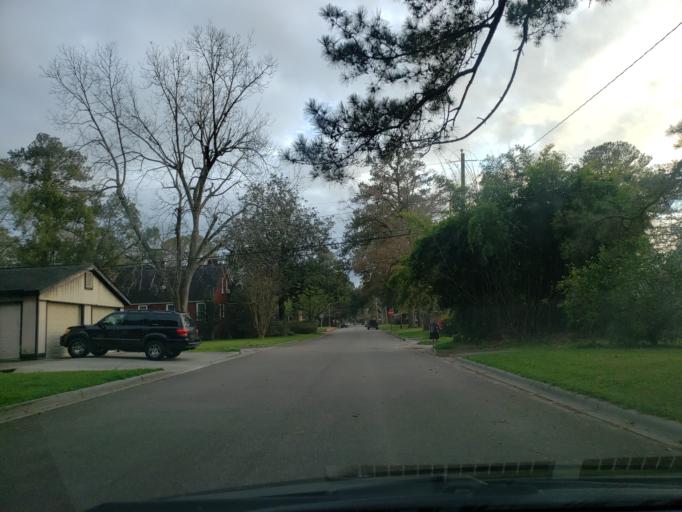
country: US
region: Georgia
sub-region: Chatham County
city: Savannah
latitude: 32.0388
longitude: -81.0955
